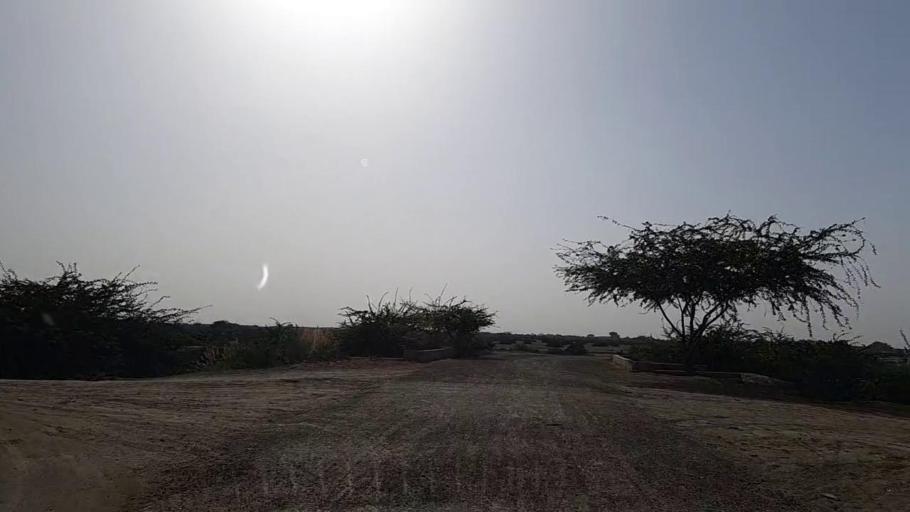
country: PK
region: Sindh
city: Jati
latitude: 24.2803
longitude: 68.2290
